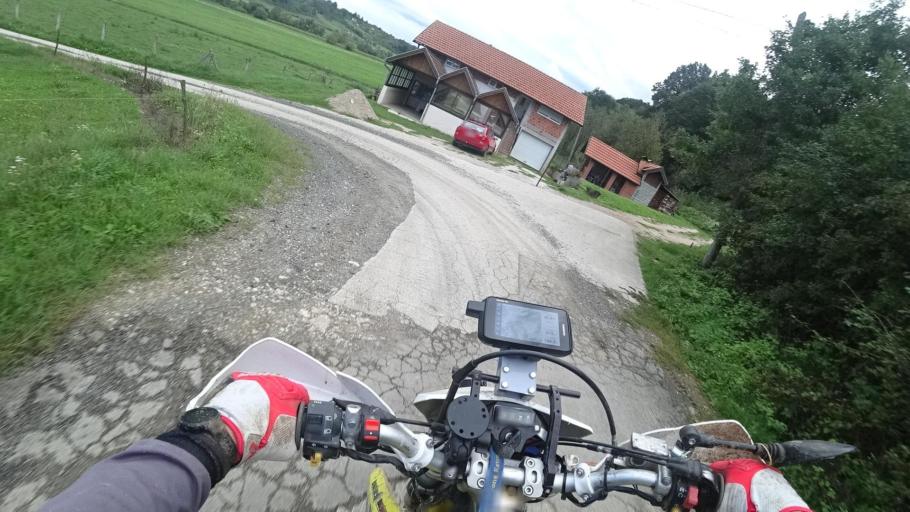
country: BA
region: Republika Srpska
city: Starcevica
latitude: 44.6685
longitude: 17.2408
